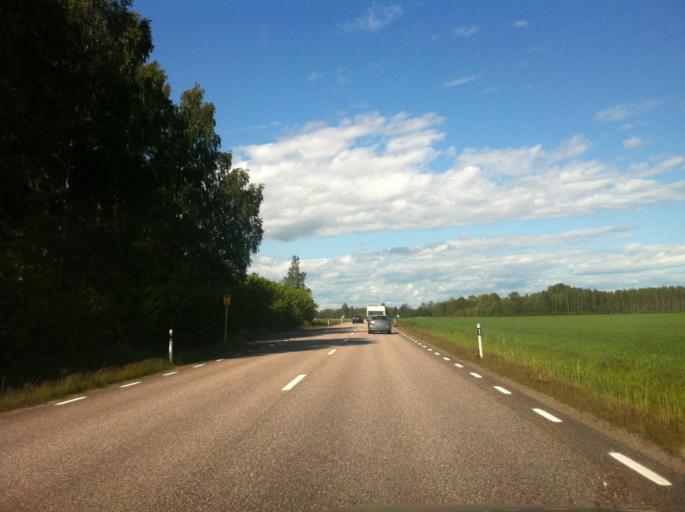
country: SE
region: Vaestra Goetaland
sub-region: Gullspangs Kommun
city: Gullspang
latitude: 59.1108
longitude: 14.1744
